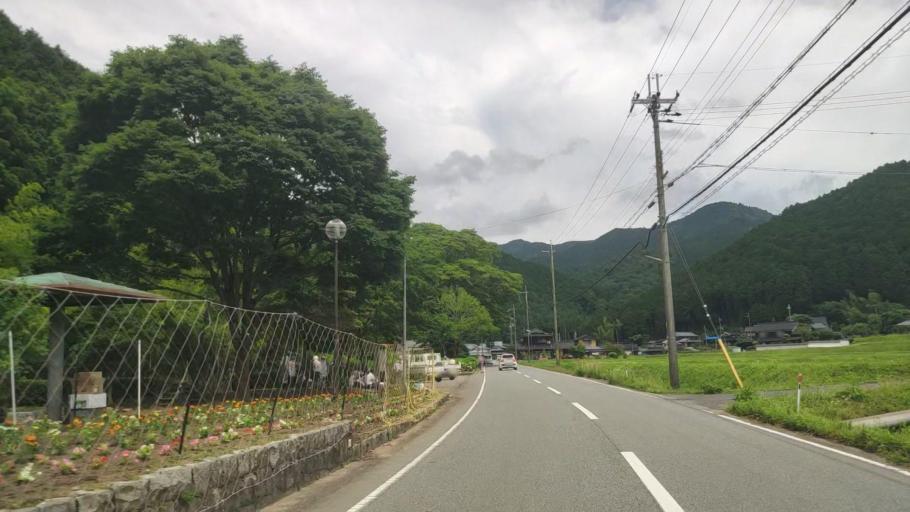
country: JP
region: Hyogo
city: Nishiwaki
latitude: 35.1840
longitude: 134.9324
